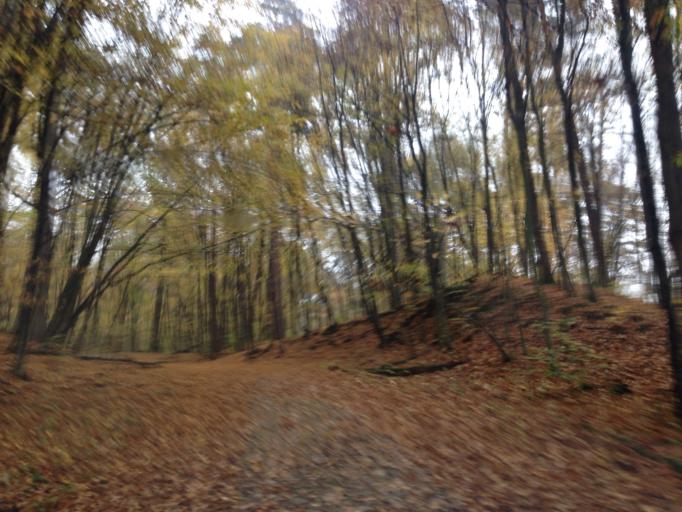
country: PL
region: Kujawsko-Pomorskie
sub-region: Powiat brodnicki
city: Gorzno
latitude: 53.2316
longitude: 19.7187
